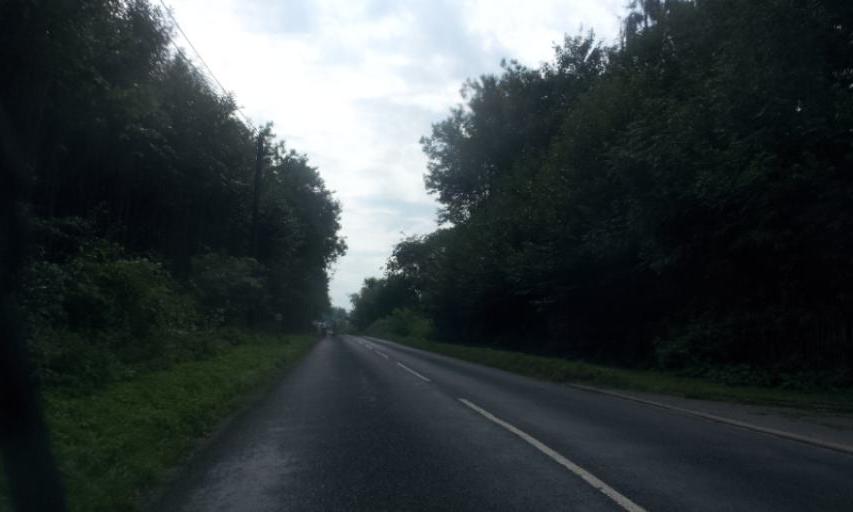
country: GB
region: England
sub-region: Kent
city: Wateringbury
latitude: 51.2711
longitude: 0.4312
